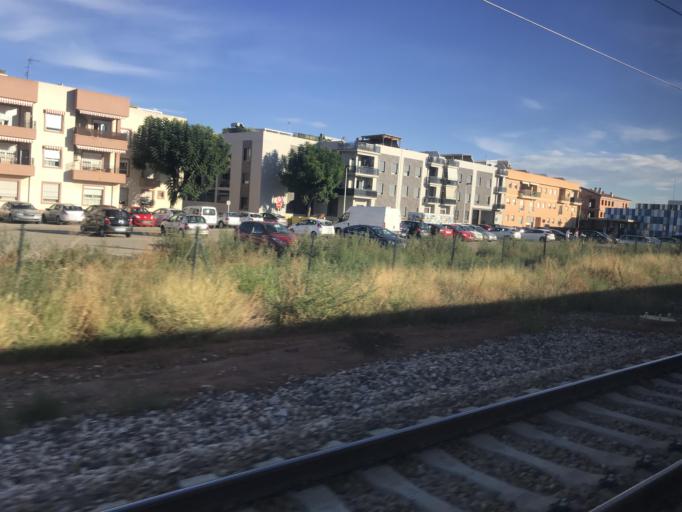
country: ES
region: Valencia
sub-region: Provincia de Valencia
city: Pucol
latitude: 39.6146
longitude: -0.3066
